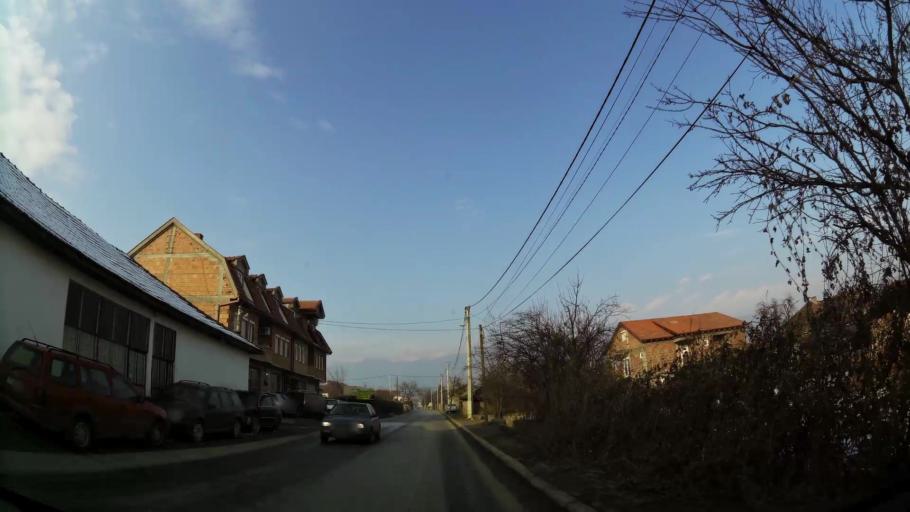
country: MK
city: Creshevo
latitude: 42.0217
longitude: 21.5147
